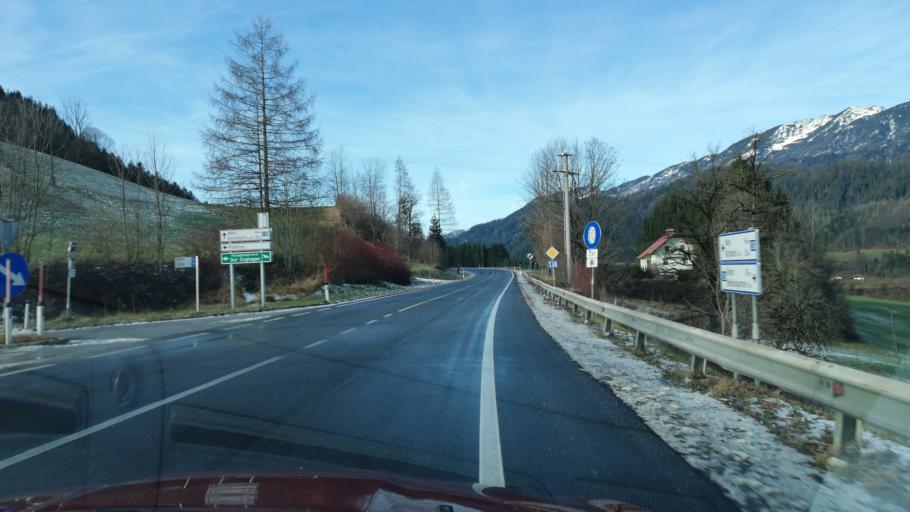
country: AT
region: Upper Austria
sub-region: Politischer Bezirk Kirchdorf an der Krems
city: Rossleithen
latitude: 47.7369
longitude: 14.2732
